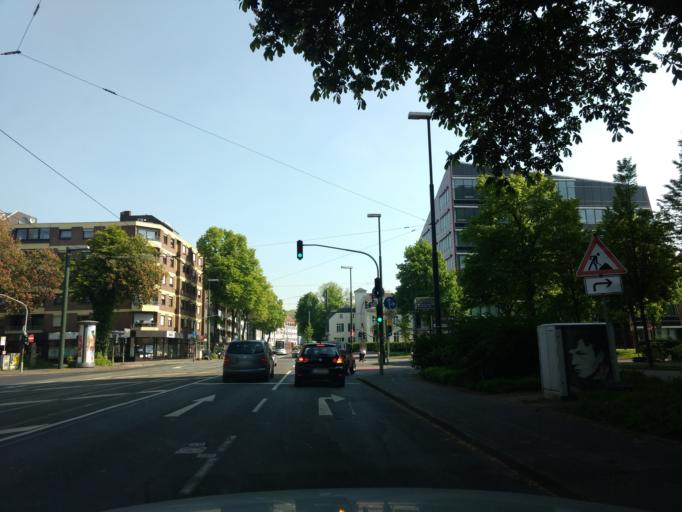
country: DE
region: North Rhine-Westphalia
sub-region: Regierungsbezirk Dusseldorf
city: Dusseldorf
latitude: 51.2380
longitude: 6.8223
